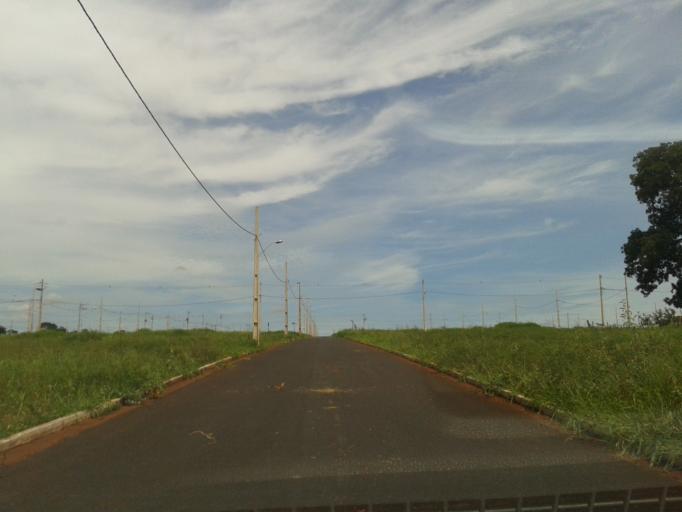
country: BR
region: Minas Gerais
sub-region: Santa Vitoria
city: Santa Vitoria
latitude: -18.8397
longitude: -50.1352
